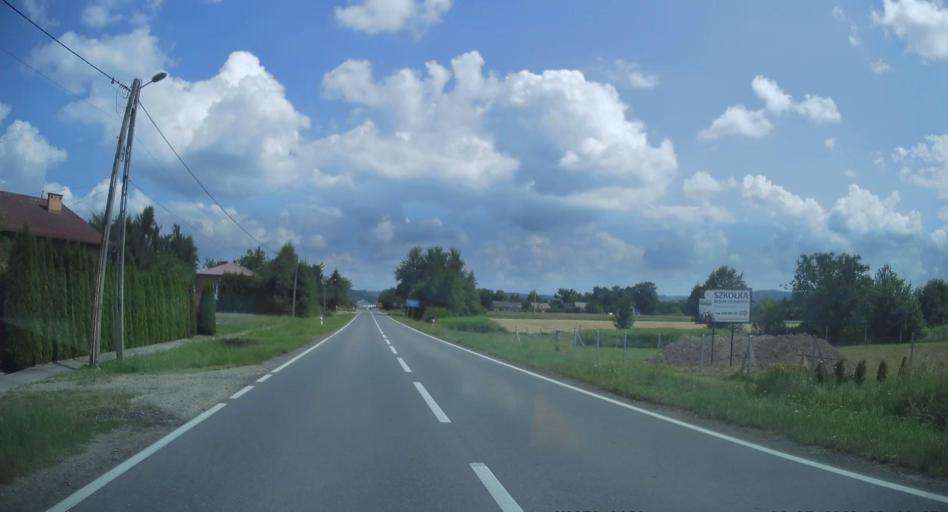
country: PL
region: Lesser Poland Voivodeship
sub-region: Powiat tarnowski
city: Zakliczyn
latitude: 49.8521
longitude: 20.8112
